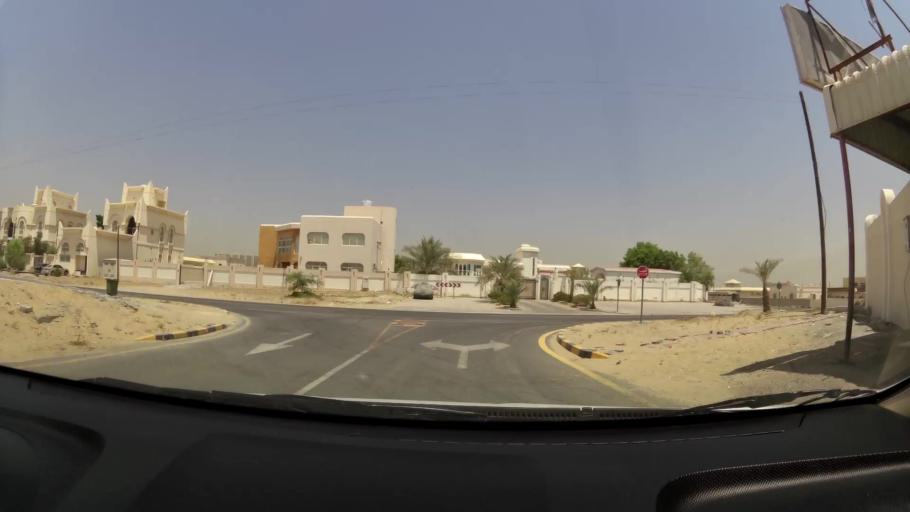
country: AE
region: Ajman
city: Ajman
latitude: 25.4024
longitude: 55.5181
